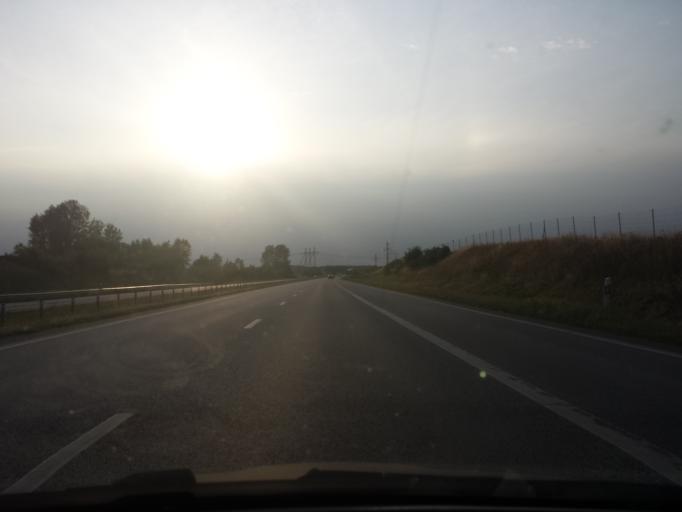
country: SE
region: Skane
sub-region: Svedala Kommun
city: Svedala
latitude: 55.5293
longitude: 13.1979
